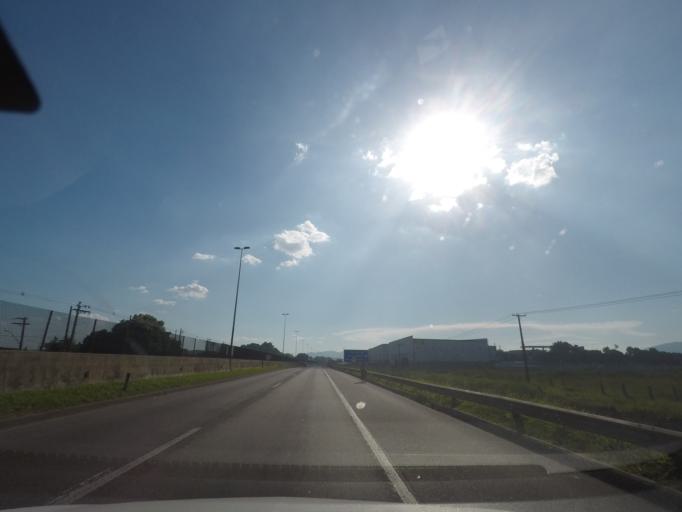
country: BR
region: Rio de Janeiro
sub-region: Duque De Caxias
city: Duque de Caxias
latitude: -22.6628
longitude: -43.2564
